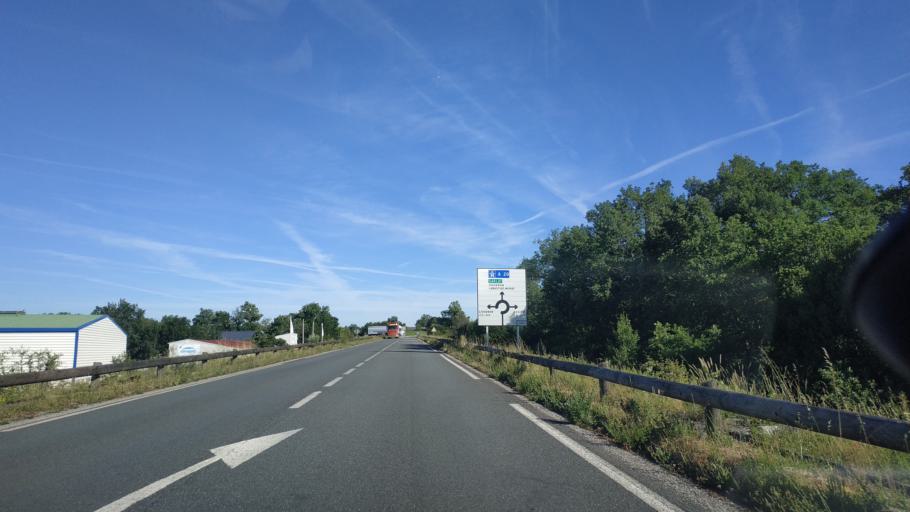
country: FR
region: Midi-Pyrenees
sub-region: Departement du Lot
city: Lacapelle-Marival
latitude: 44.6549
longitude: 1.8541
